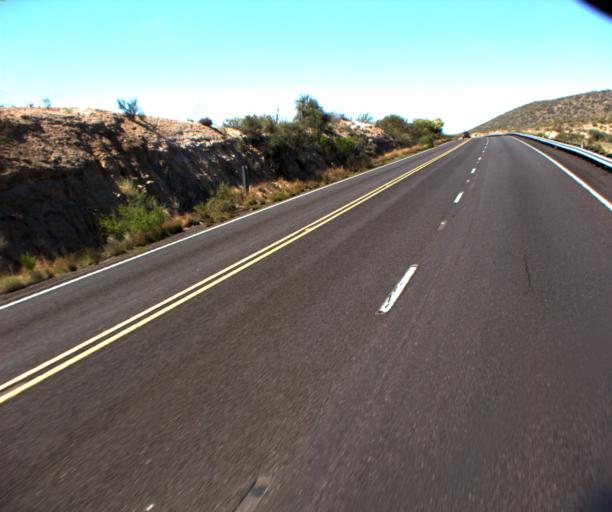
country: US
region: Arizona
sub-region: Mohave County
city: Kingman
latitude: 34.9269
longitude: -113.6586
